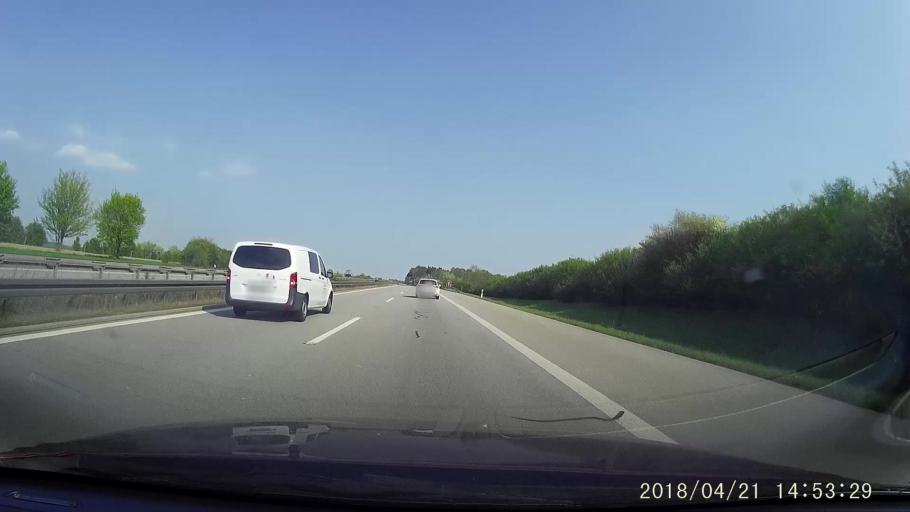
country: DE
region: Saxony
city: Guttau
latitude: 51.2090
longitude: 14.5845
